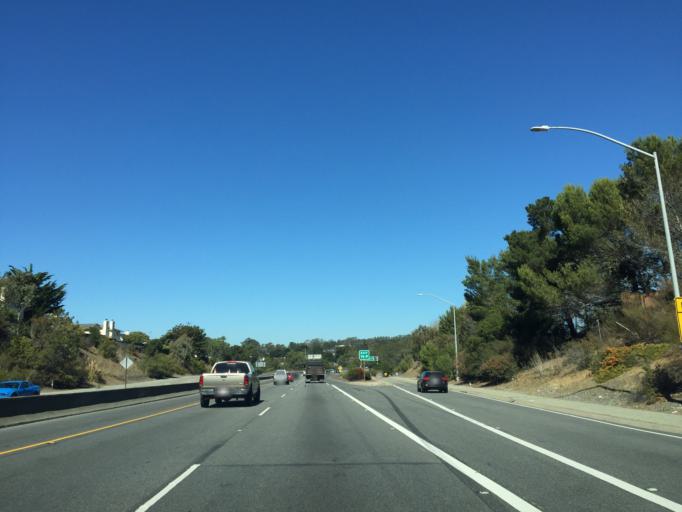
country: US
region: California
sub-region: San Mateo County
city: Highlands-Baywood Park
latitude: 37.5193
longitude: -122.3307
